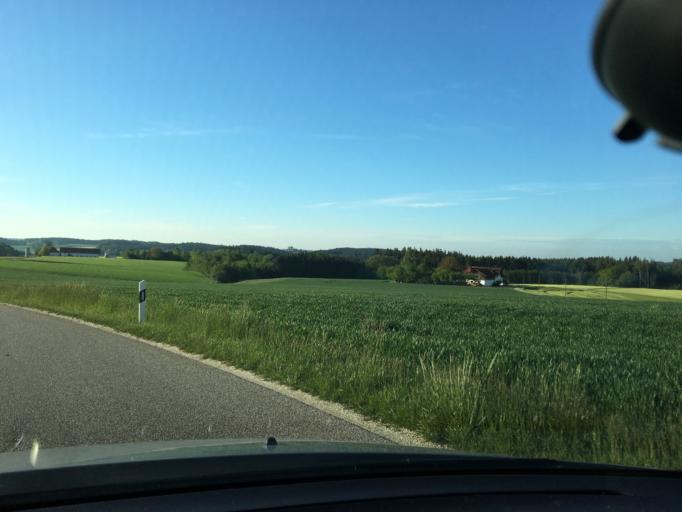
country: DE
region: Bavaria
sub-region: Lower Bavaria
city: Vilsbiburg
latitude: 48.5101
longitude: 12.3295
